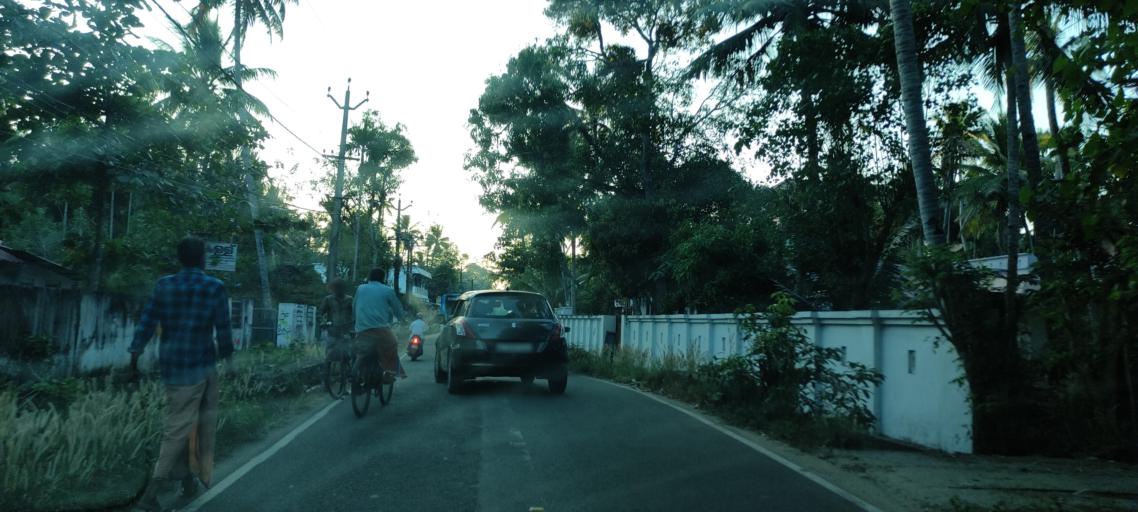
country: IN
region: Kerala
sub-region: Alappuzha
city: Kayankulam
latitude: 9.2595
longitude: 76.4419
